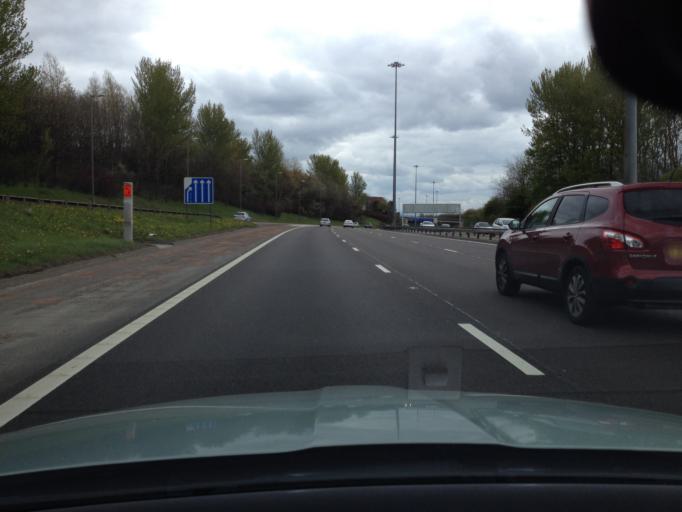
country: GB
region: Scotland
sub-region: North Lanarkshire
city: Stepps
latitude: 55.8714
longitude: -4.1788
